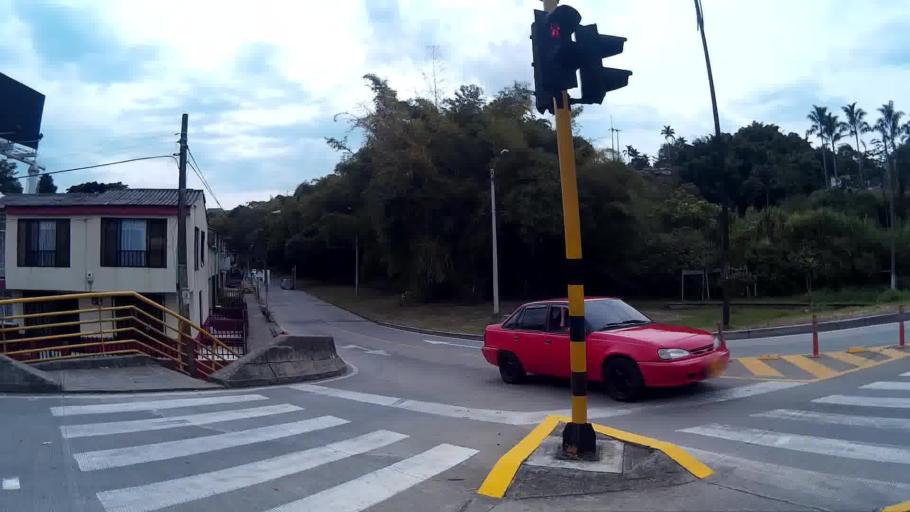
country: CO
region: Risaralda
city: Pereira
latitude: 4.8090
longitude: -75.7356
